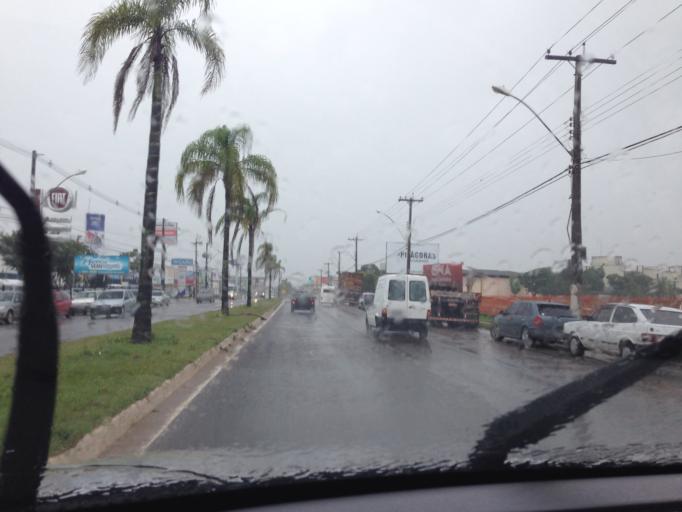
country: BR
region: Espirito Santo
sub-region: Guarapari
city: Guarapari
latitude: -20.6554
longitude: -40.5033
